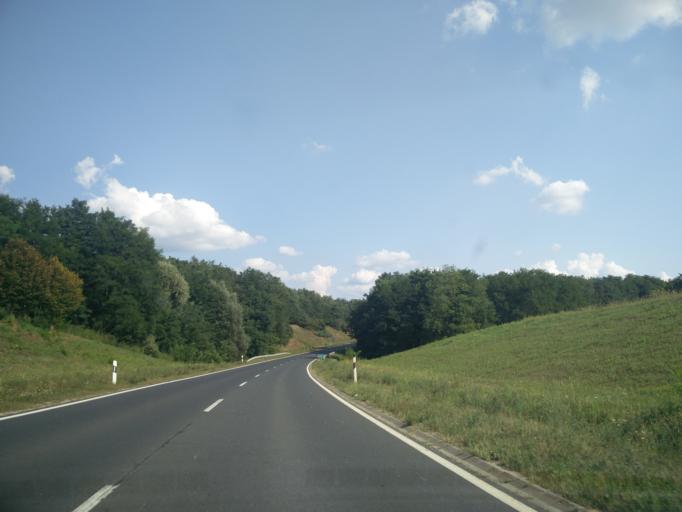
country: HU
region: Zala
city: Zalaegerszeg
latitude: 46.8789
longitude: 16.8476
